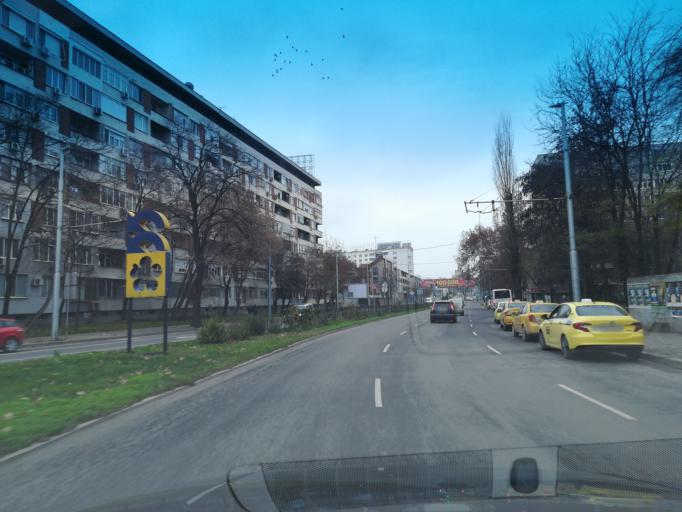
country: BG
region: Plovdiv
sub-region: Obshtina Plovdiv
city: Plovdiv
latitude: 42.1626
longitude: 24.7474
